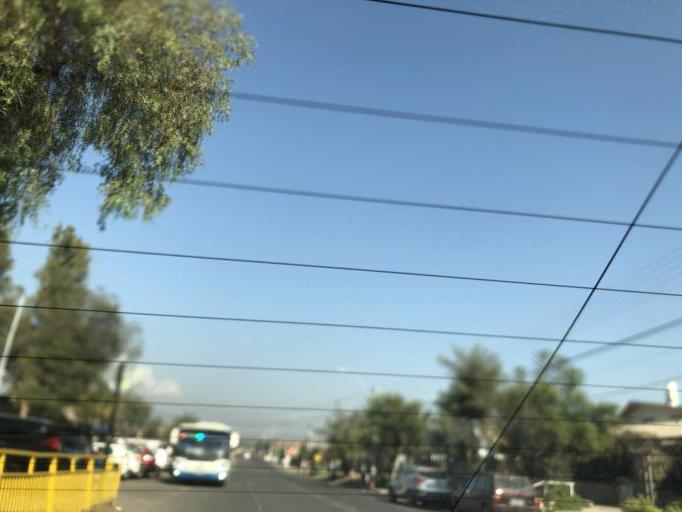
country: CL
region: Santiago Metropolitan
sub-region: Provincia de Cordillera
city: Puente Alto
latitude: -33.6146
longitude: -70.5637
